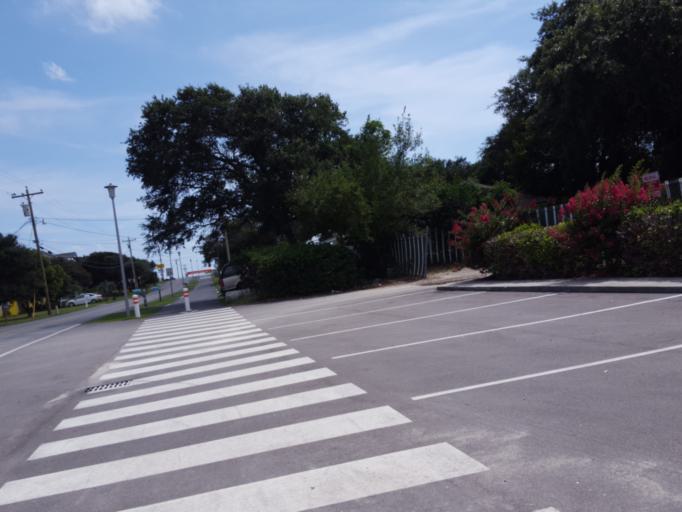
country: US
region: North Carolina
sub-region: Carteret County
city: Cape Carteret
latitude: 34.6644
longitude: -77.0349
